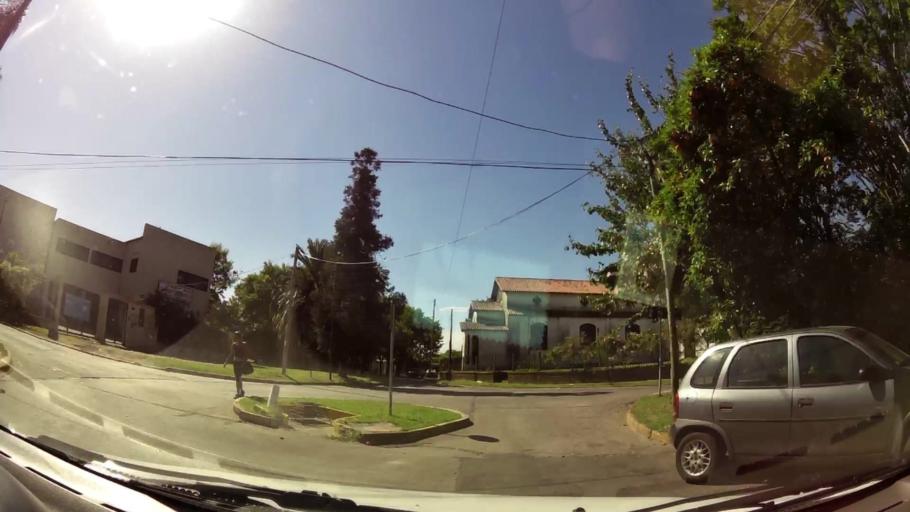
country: AR
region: Buenos Aires
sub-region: Partido de San Isidro
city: San Isidro
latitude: -34.4715
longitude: -58.5308
